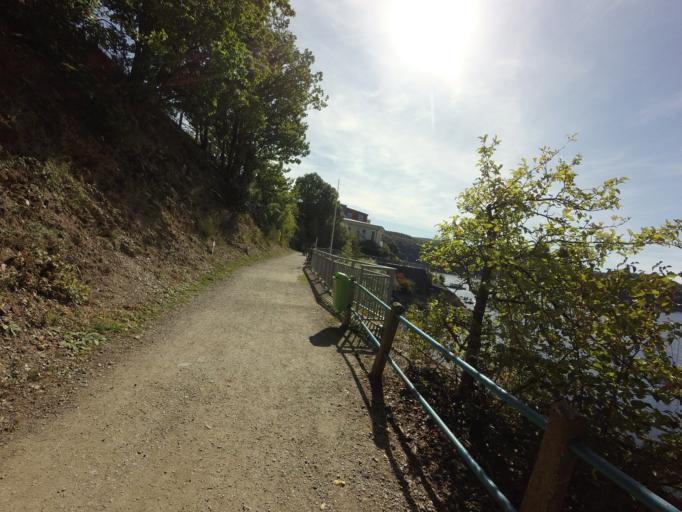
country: DE
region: North Rhine-Westphalia
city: Heimbach
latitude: 50.6412
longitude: 6.4419
